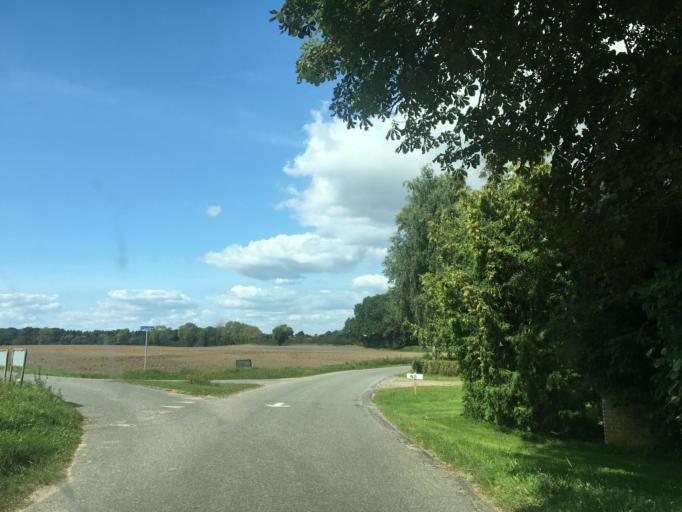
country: DK
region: South Denmark
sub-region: Middelfart Kommune
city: Ejby
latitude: 55.3948
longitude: 9.9233
